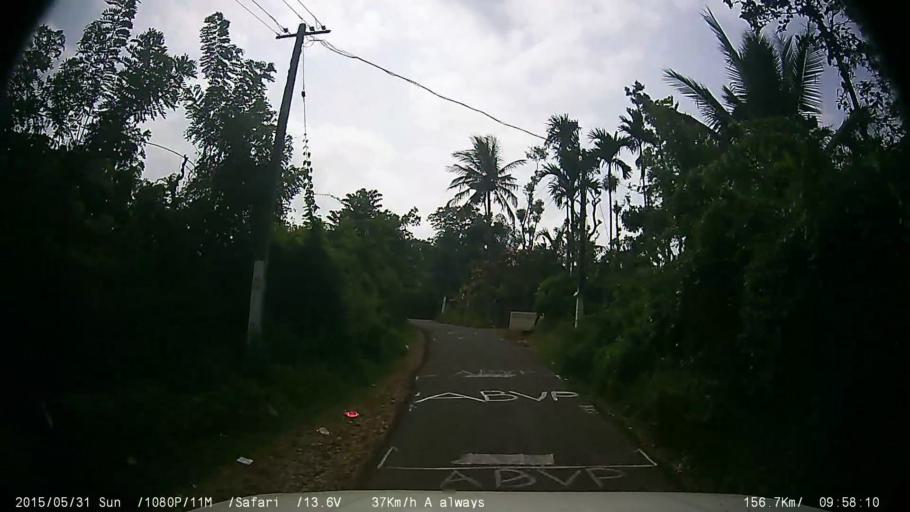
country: IN
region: Kerala
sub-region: Wayanad
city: Kalpetta
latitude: 11.5921
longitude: 76.0615
